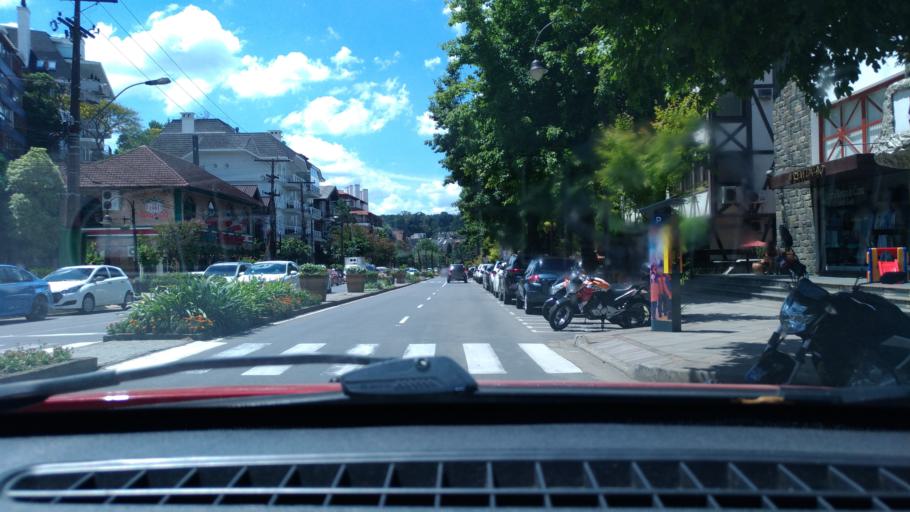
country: BR
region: Rio Grande do Sul
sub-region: Canela
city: Canela
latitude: -29.3842
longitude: -50.8726
